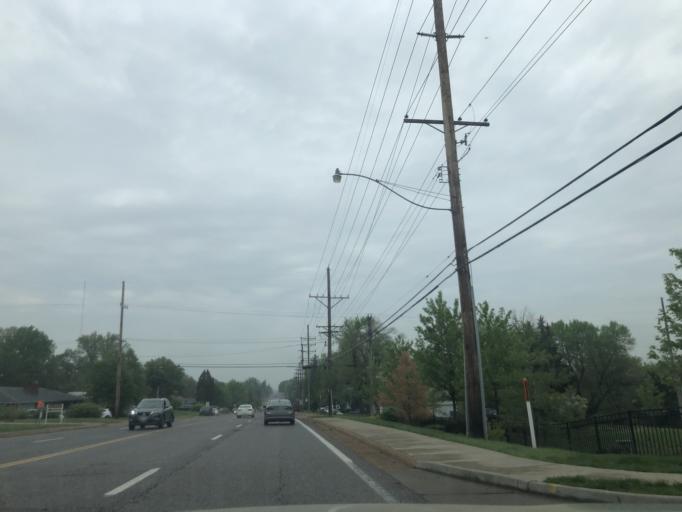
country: US
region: Missouri
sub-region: Saint Louis County
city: Affton
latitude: 38.5596
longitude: -90.3218
